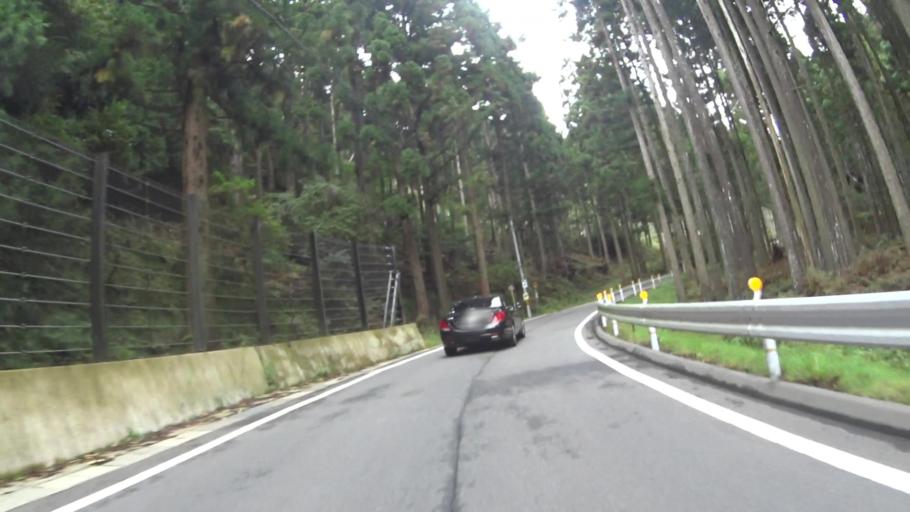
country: JP
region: Kyoto
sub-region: Kyoto-shi
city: Kamigyo-ku
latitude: 35.1416
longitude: 135.7805
